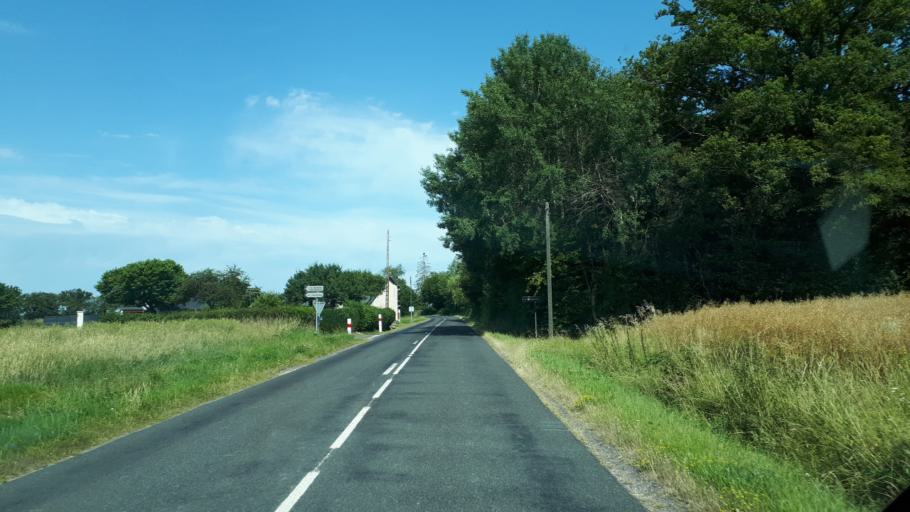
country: FR
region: Centre
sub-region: Departement du Loir-et-Cher
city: La Ville-aux-Clercs
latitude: 47.9627
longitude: 1.0669
